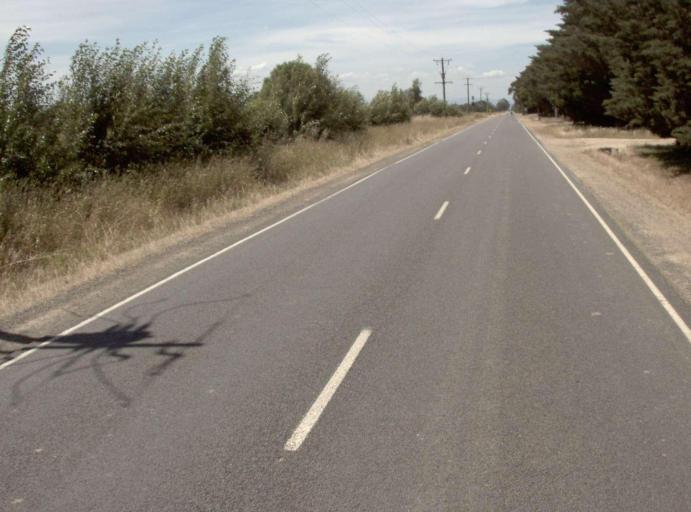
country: AU
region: Victoria
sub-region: Wellington
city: Heyfield
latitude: -38.0582
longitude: 146.8734
